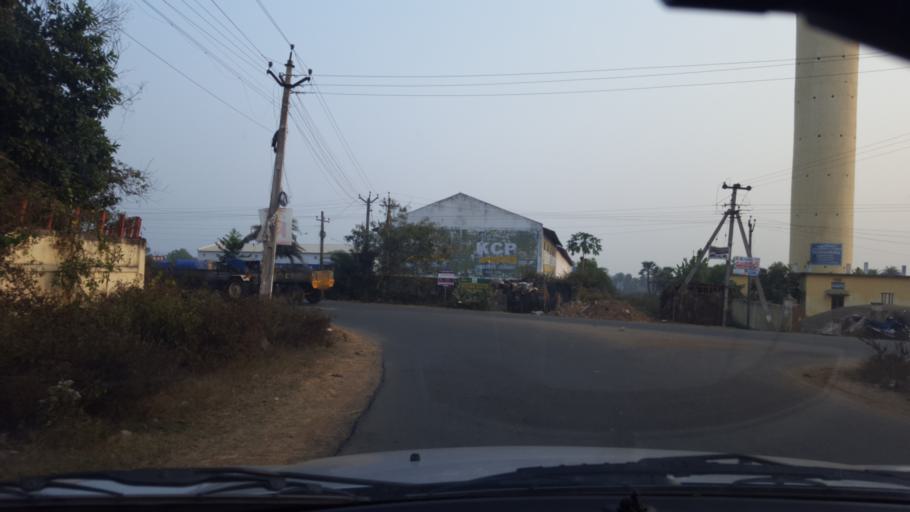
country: IN
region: Andhra Pradesh
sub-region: Srikakulam
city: Amudalavalasa
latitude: 18.3851
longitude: 83.9237
